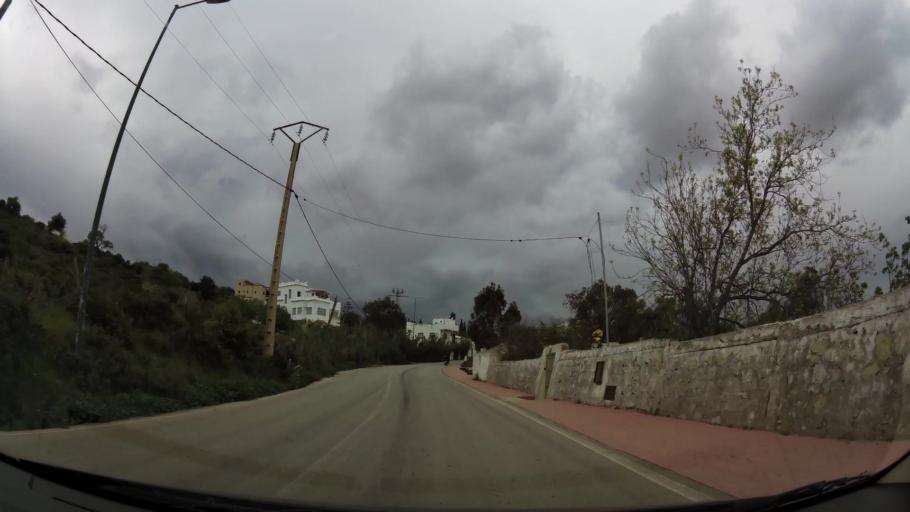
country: MA
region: Tanger-Tetouan
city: Tetouan
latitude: 35.5510
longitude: -5.3638
